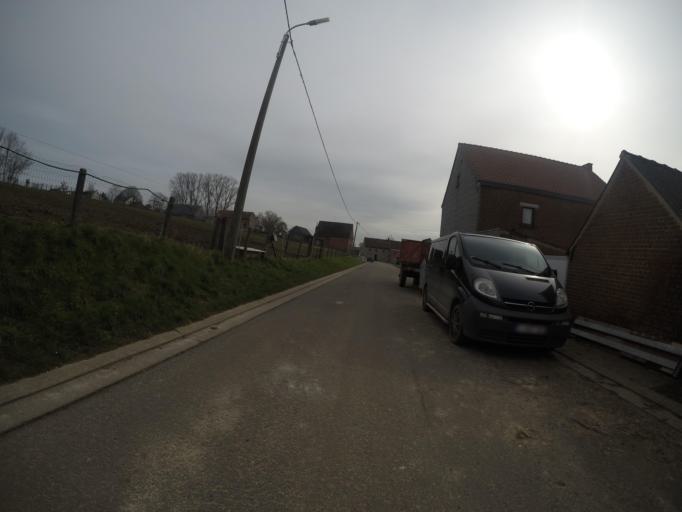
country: BE
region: Flanders
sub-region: Provincie Oost-Vlaanderen
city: Sint-Maria-Lierde
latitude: 50.8305
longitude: 3.8487
